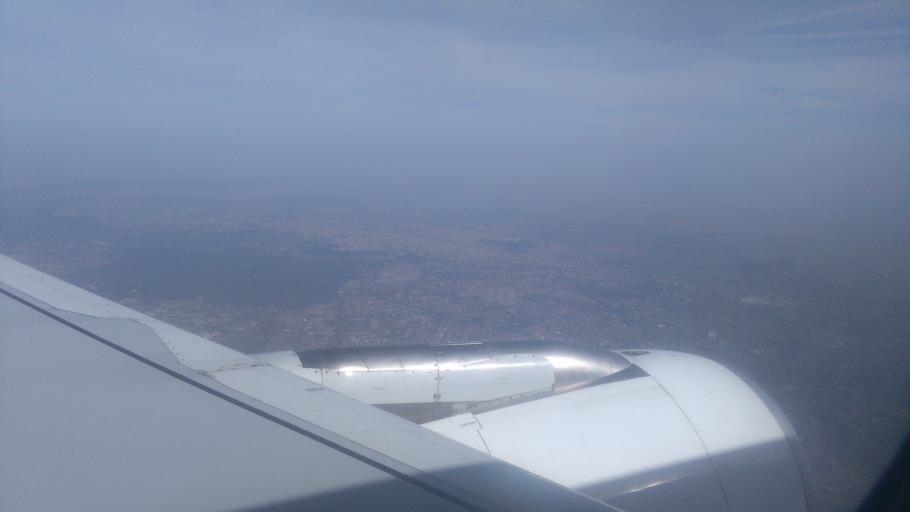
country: ES
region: Madrid
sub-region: Provincia de Madrid
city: Mostoles
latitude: 40.3350
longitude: -3.8477
